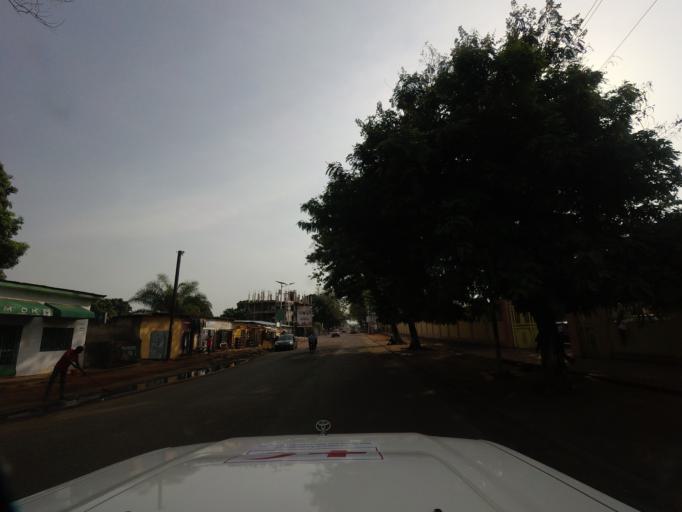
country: GN
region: Conakry
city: Conakry
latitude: 9.5458
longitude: -13.6778
